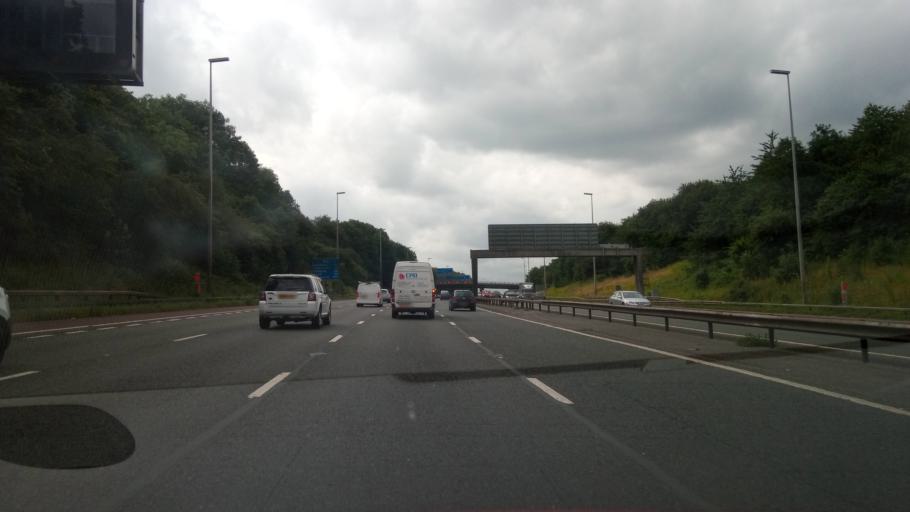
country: GB
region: England
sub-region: Lancashire
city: Clayton-le-Woods
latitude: 53.7574
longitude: -2.6372
